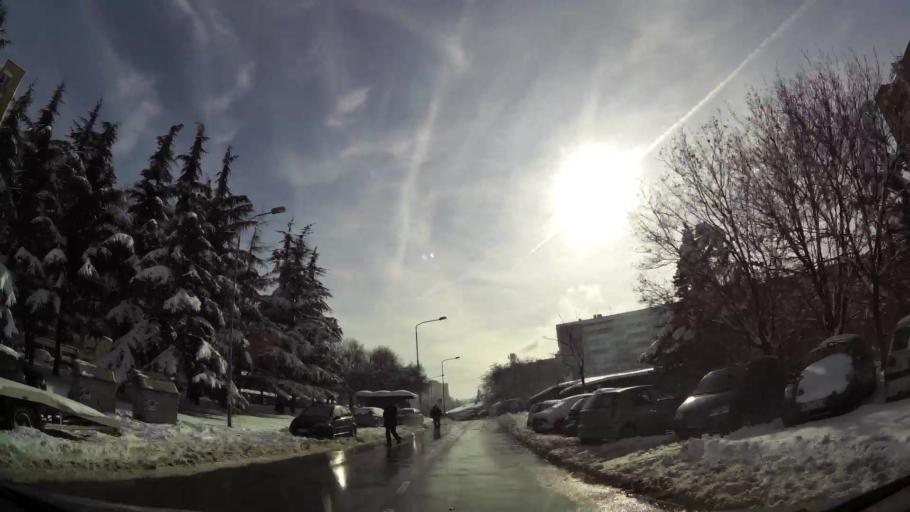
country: RS
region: Central Serbia
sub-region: Belgrade
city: Zvezdara
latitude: 44.7920
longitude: 20.5326
